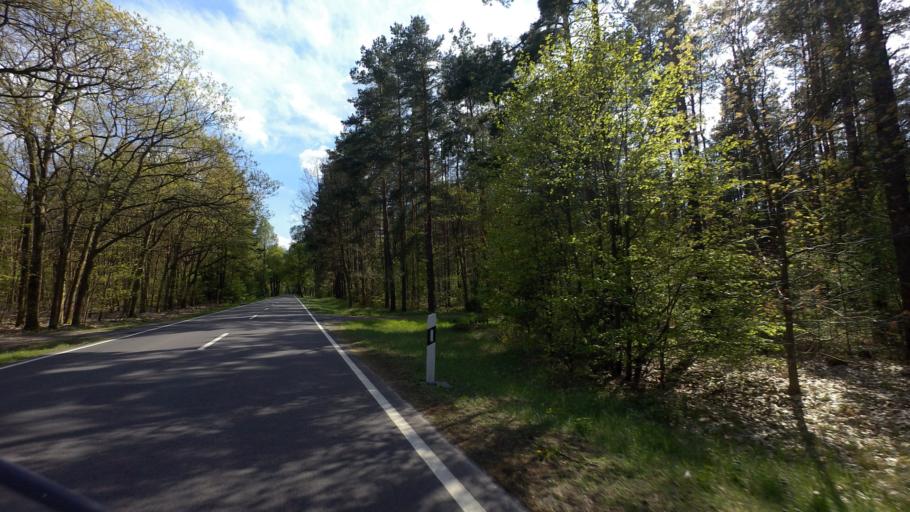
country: DE
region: Brandenburg
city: Milmersdorf
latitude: 53.0290
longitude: 13.6035
